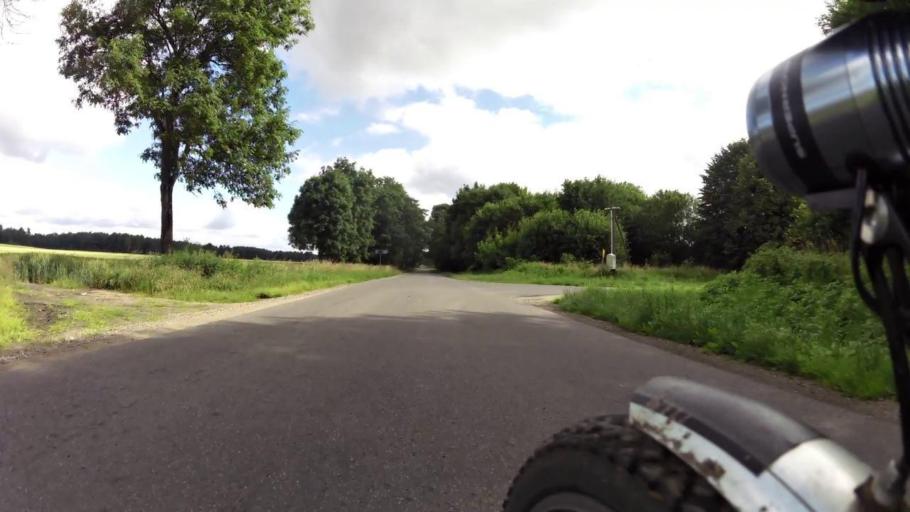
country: PL
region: West Pomeranian Voivodeship
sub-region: Powiat swidwinski
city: Rabino
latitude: 53.7958
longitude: 15.9069
